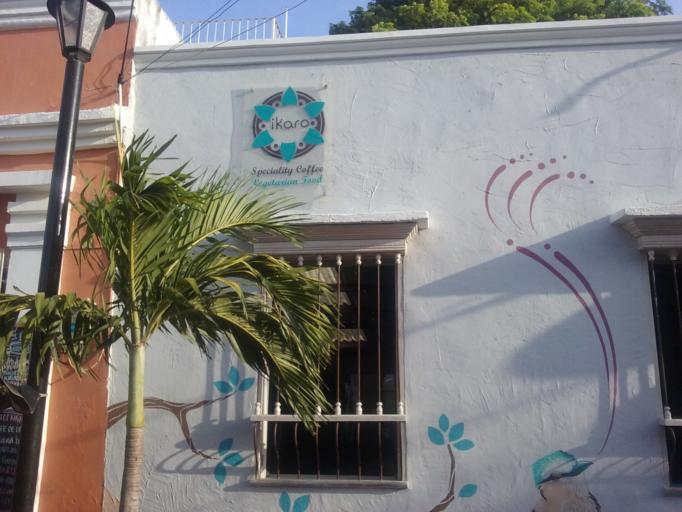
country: CO
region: Magdalena
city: Santa Marta
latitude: 11.2423
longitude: -74.2123
